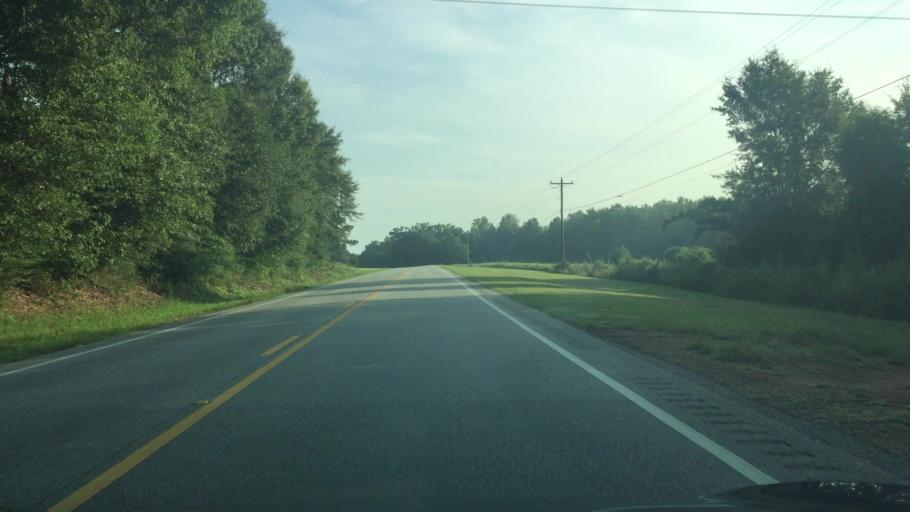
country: US
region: Alabama
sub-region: Covington County
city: Andalusia
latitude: 31.1509
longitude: -86.4588
